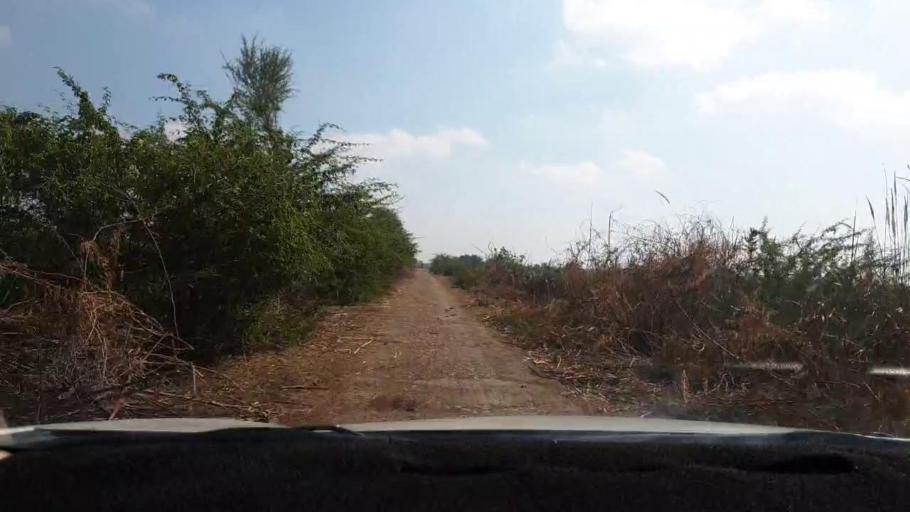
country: PK
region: Sindh
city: Berani
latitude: 25.7643
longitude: 68.8649
